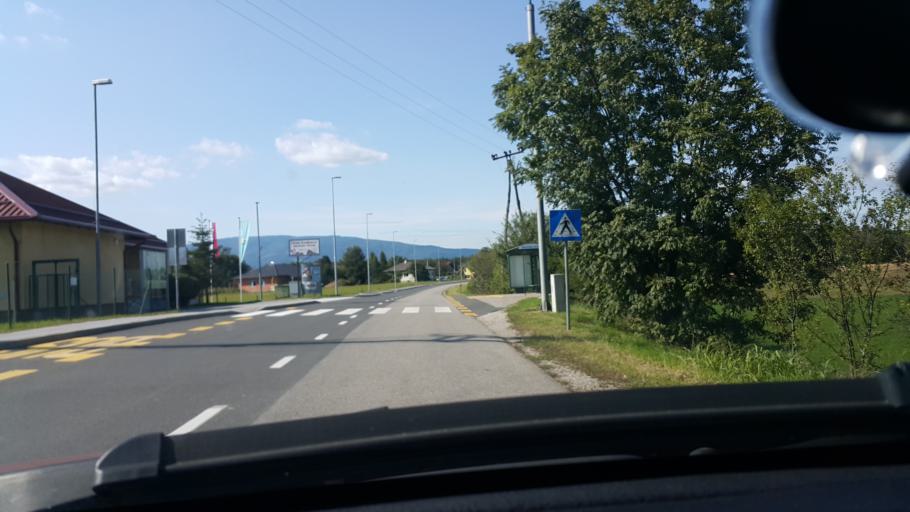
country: SI
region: Race-Fram
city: Race
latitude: 46.4660
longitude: 15.7159
